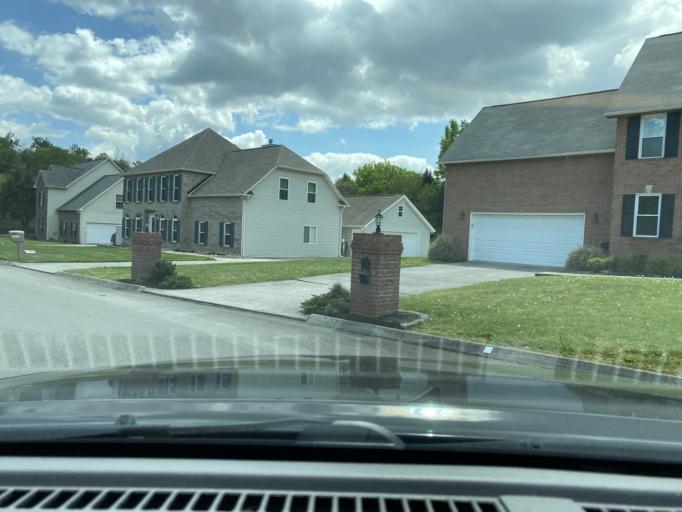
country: US
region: Tennessee
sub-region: Knox County
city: Farragut
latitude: 35.9508
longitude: -84.1129
